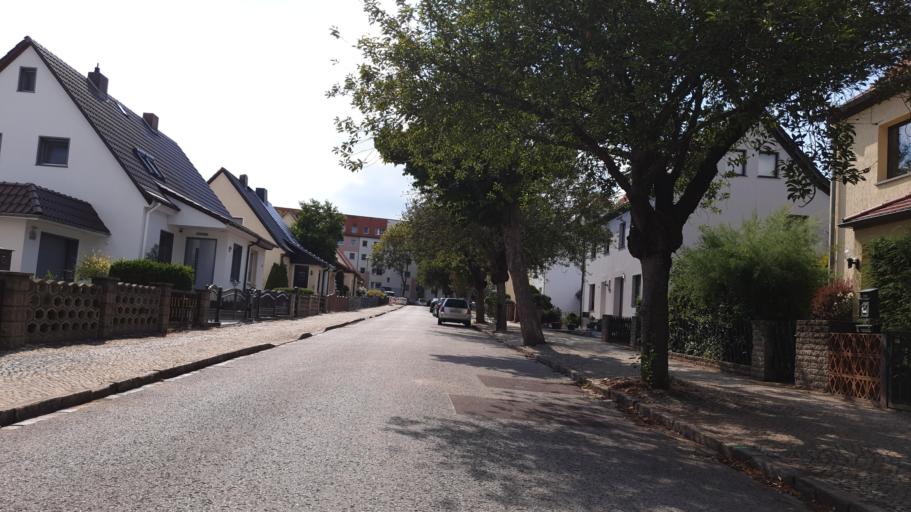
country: DE
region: Saxony-Anhalt
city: Bernburg
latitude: 51.7851
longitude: 11.7560
